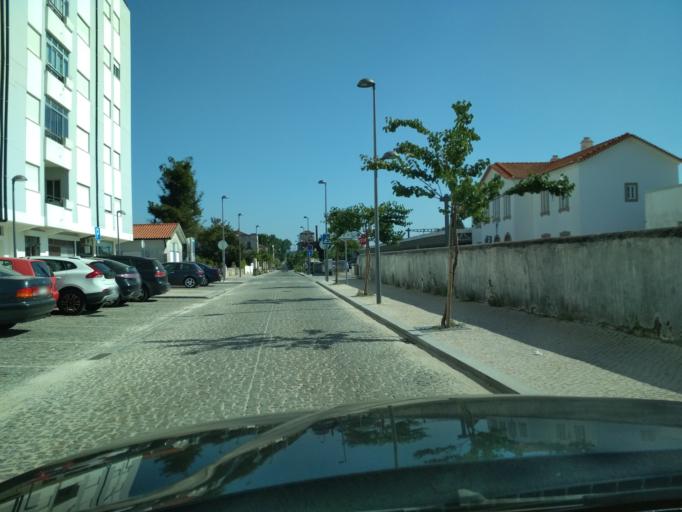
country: PT
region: Aveiro
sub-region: Mealhada
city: Mealhada
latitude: 40.3759
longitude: -8.4535
